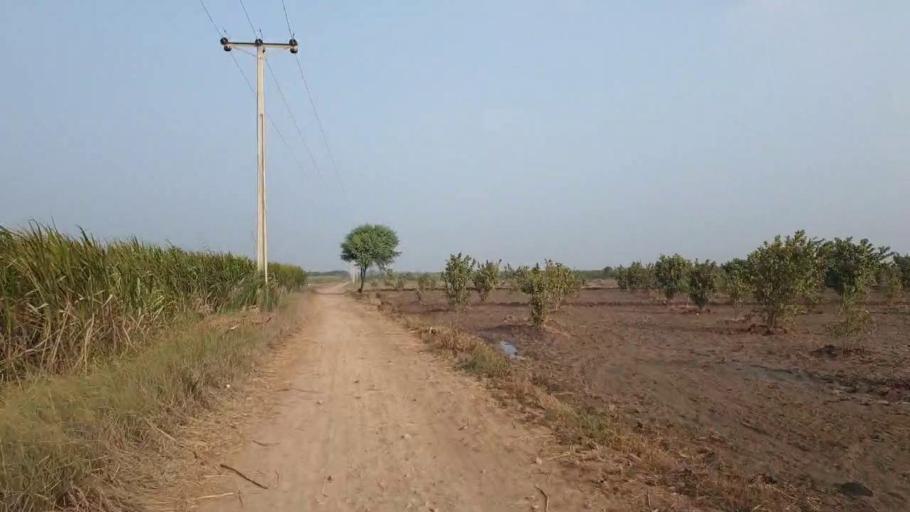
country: PK
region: Sindh
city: Tando Muhammad Khan
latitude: 25.1498
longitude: 68.5884
